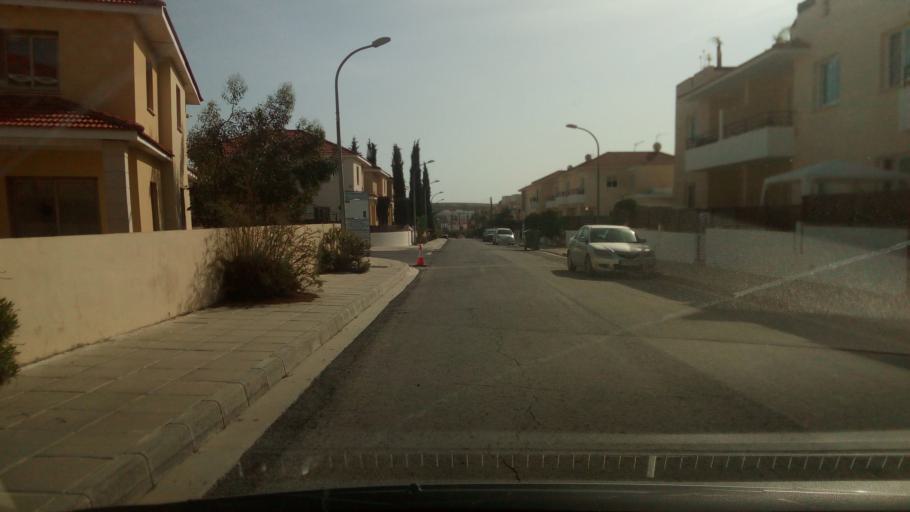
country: CY
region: Larnaka
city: Voroklini
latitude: 34.9792
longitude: 33.6501
